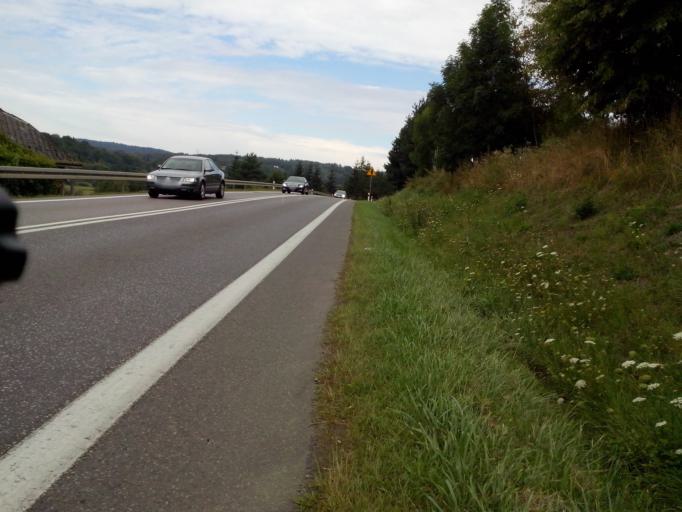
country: PL
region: Subcarpathian Voivodeship
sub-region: Powiat brzozowski
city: Jasienica Rosielna
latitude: 49.7669
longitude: 21.9563
